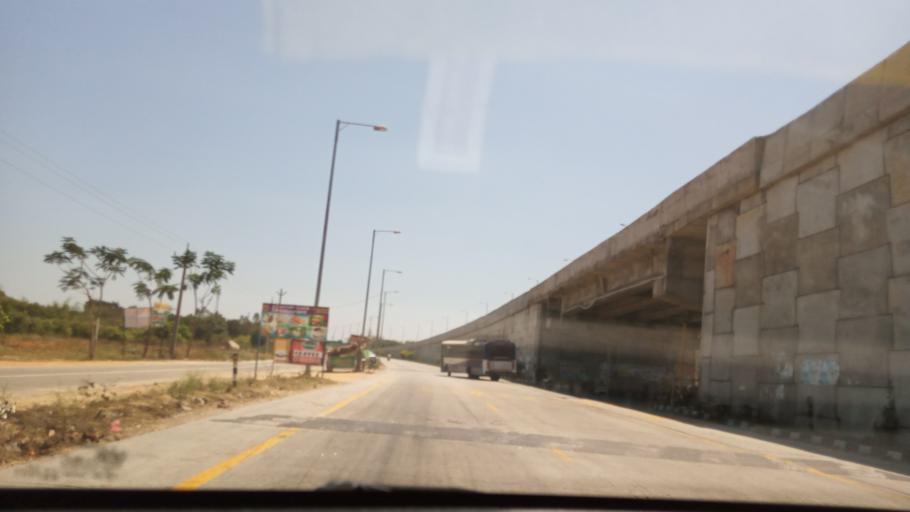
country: IN
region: Andhra Pradesh
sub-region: Chittoor
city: Chittoor
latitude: 13.2048
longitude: 78.9361
